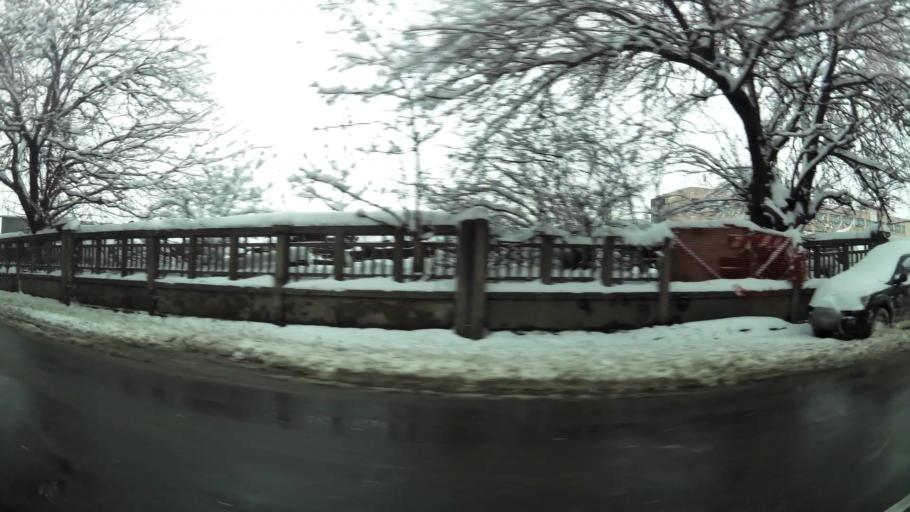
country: RS
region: Central Serbia
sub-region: Belgrade
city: Stari Grad
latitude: 44.8190
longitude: 20.4836
